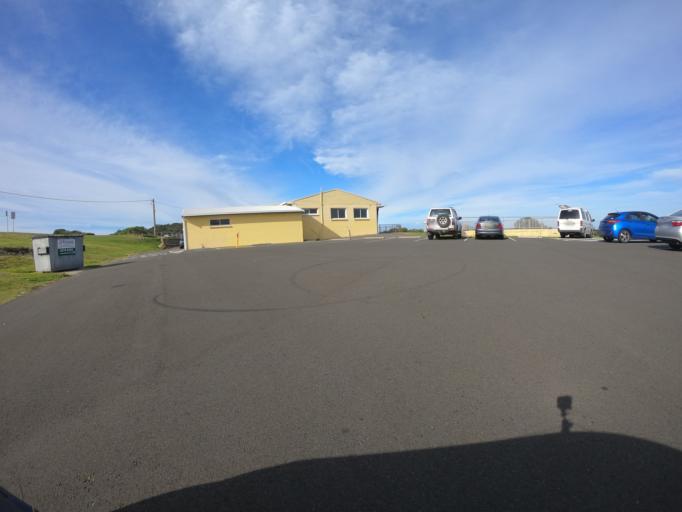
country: AU
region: New South Wales
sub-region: Wollongong
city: Port Kembla
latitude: -34.4919
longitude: 150.9072
